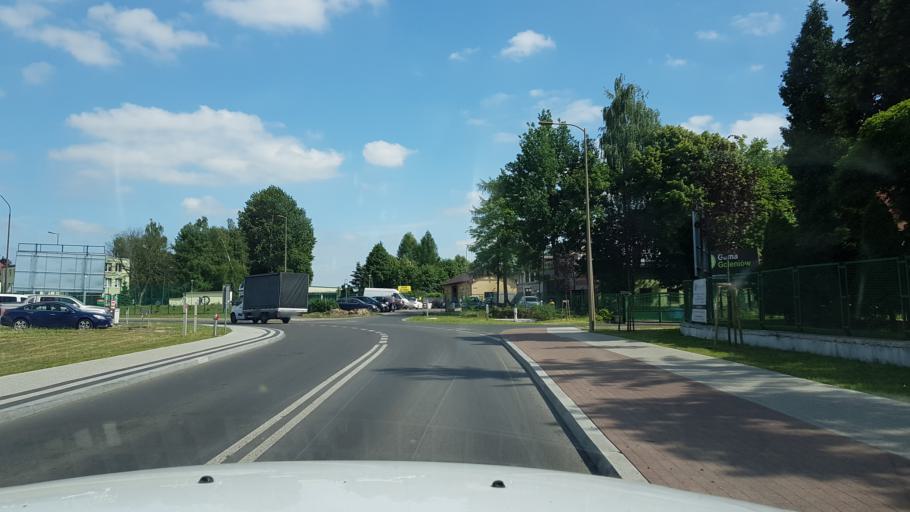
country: PL
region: West Pomeranian Voivodeship
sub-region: Powiat goleniowski
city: Goleniow
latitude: 53.5609
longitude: 14.8410
